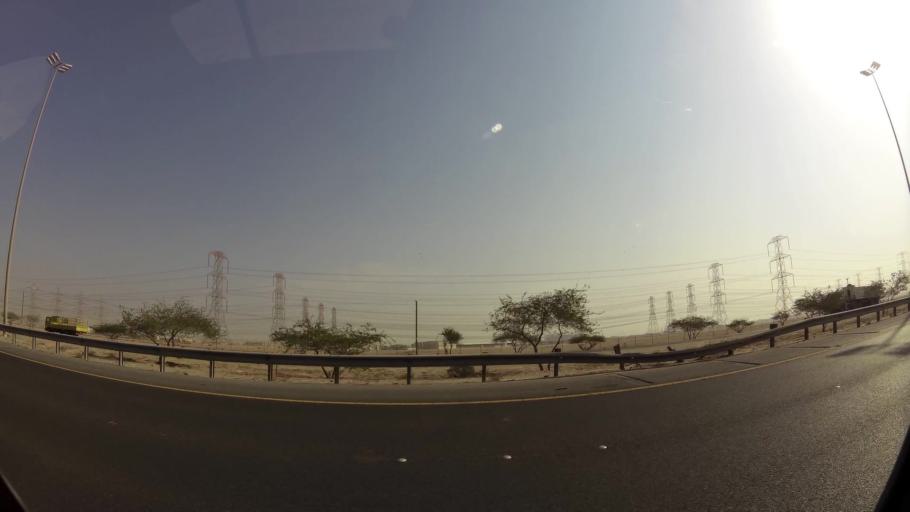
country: KW
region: Al Ahmadi
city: Al Ahmadi
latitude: 28.9852
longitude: 48.1052
